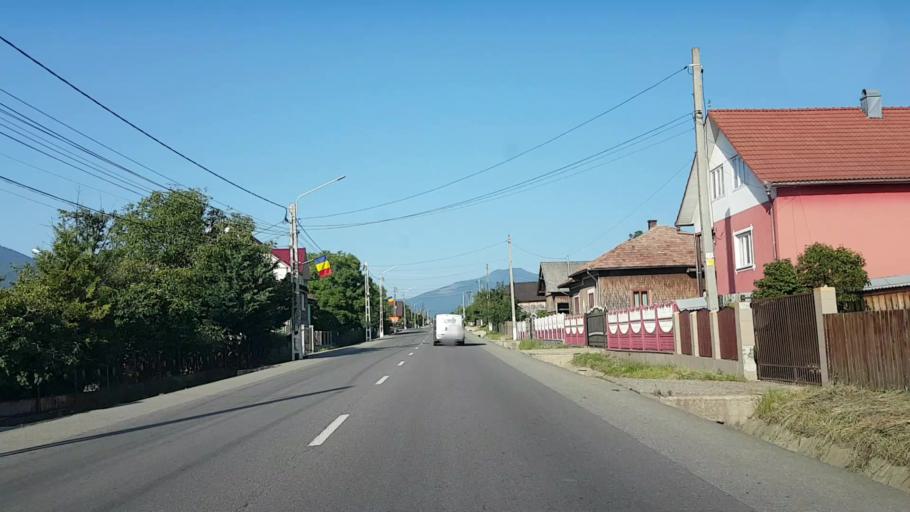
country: RO
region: Bistrita-Nasaud
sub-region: Comuna Josenii Bargaului
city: Mijlocenii Bargaului
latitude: 47.2150
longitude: 24.6958
